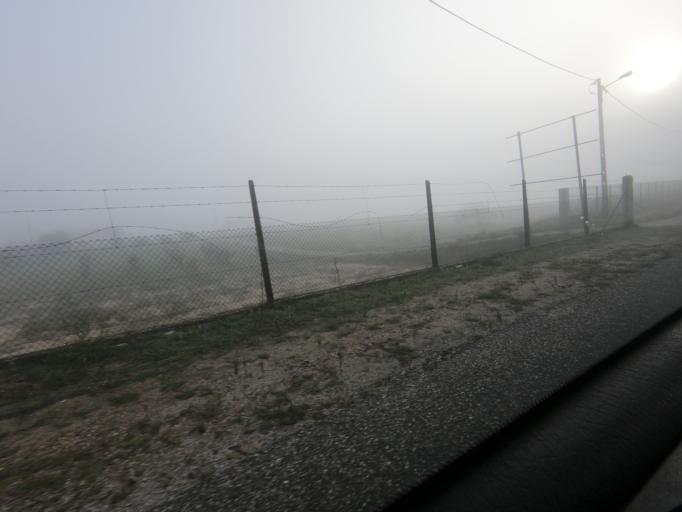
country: PT
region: Setubal
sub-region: Palmela
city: Palmela
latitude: 38.5889
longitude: -8.8372
